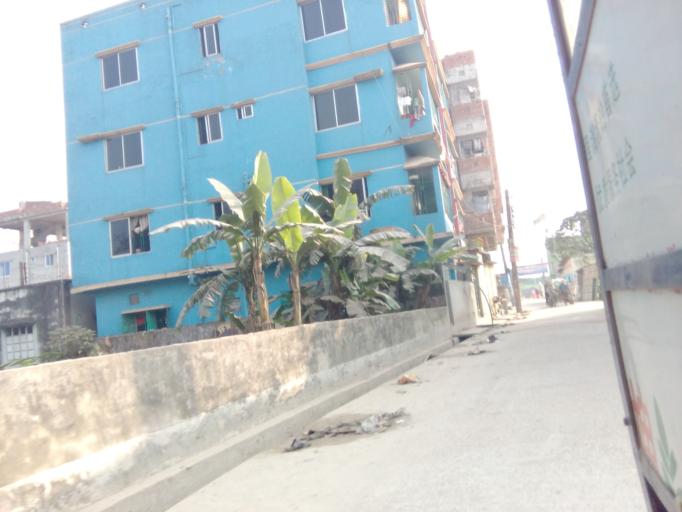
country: BD
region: Dhaka
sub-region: Dhaka
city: Dhaka
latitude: 23.7034
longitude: 90.4756
